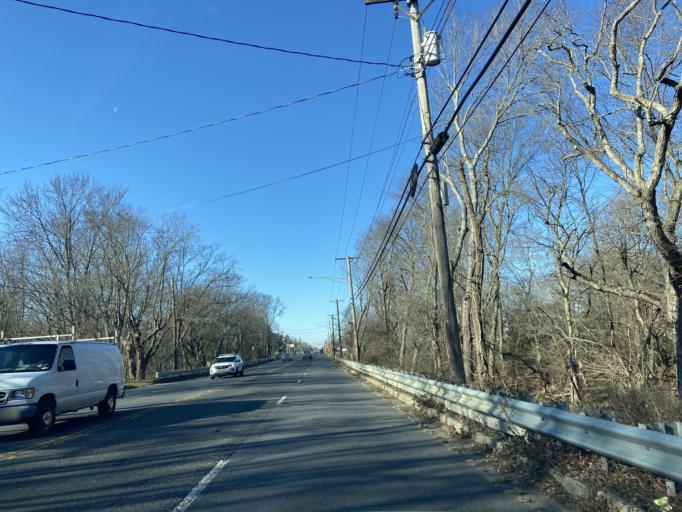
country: US
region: New Jersey
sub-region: Cumberland County
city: Vineland
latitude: 39.4877
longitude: -75.0571
